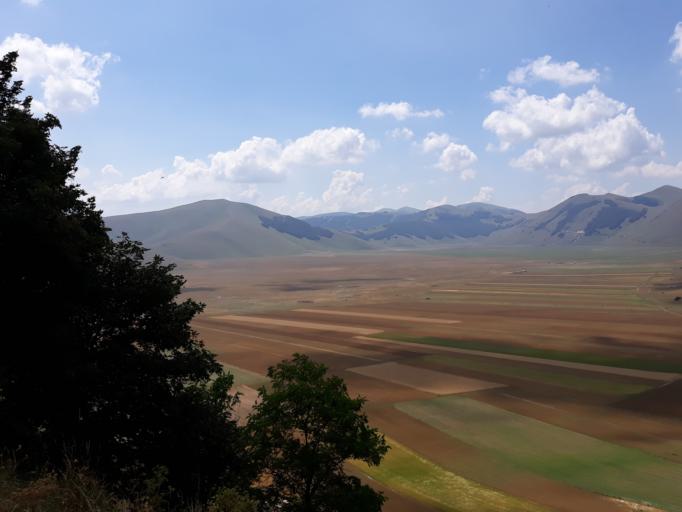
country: IT
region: The Marches
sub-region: Provincia di Macerata
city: Castelsantangelo sul Nera
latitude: 42.8279
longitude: 13.2066
